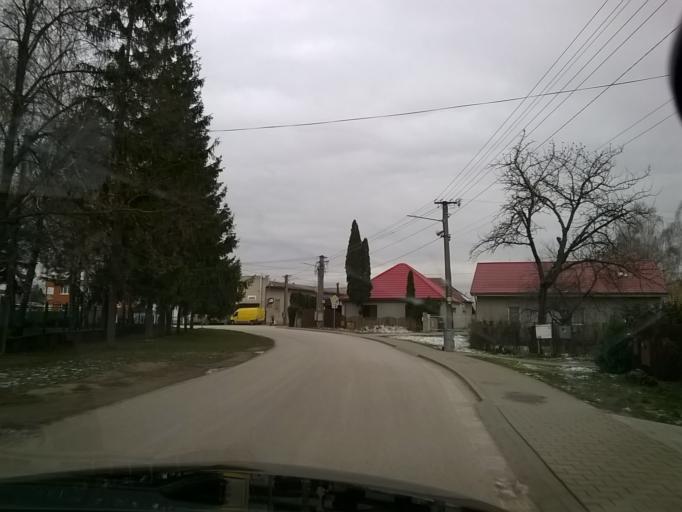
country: SK
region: Nitriansky
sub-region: Okres Nitra
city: Nitra
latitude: 48.4078
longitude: 18.0842
